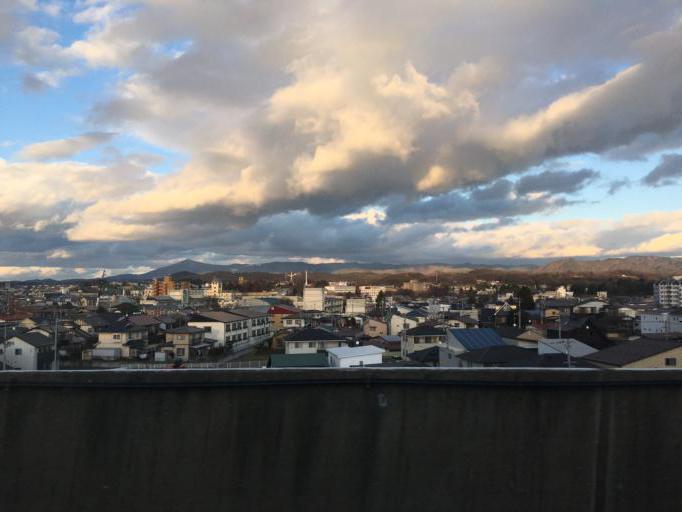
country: JP
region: Iwate
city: Morioka-shi
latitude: 39.7109
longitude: 141.1260
